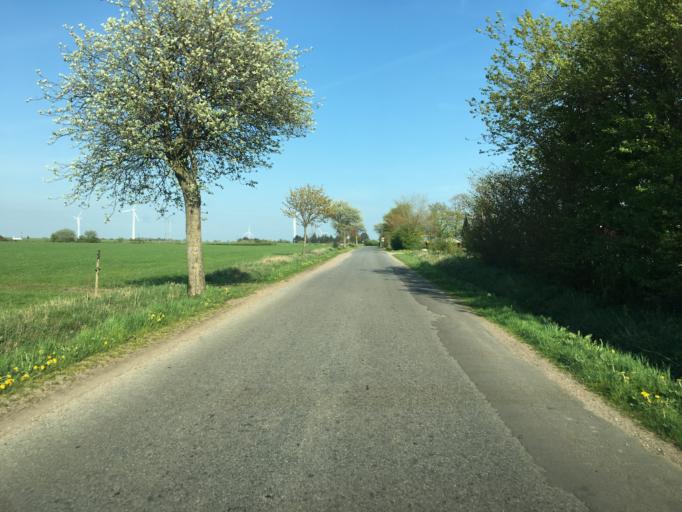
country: DK
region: South Denmark
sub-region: Aabenraa Kommune
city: Rodekro
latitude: 55.0970
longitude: 9.1872
